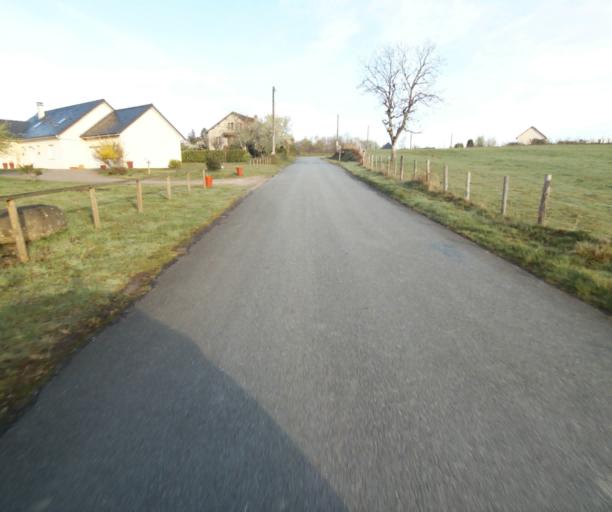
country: FR
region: Limousin
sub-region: Departement de la Correze
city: Naves
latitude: 45.3140
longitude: 1.8350
